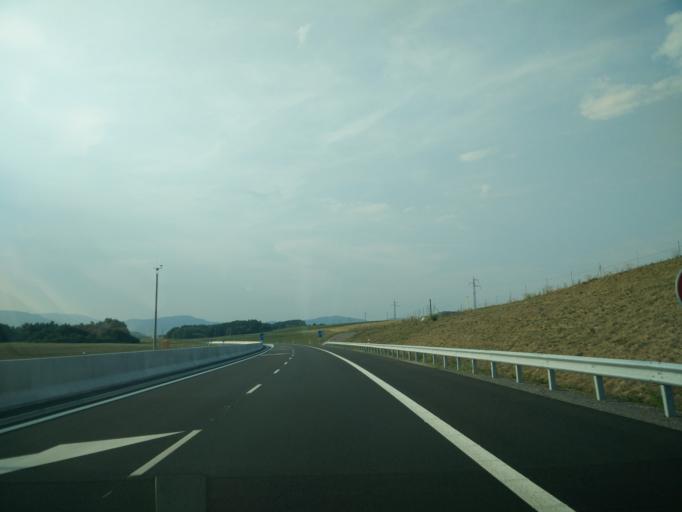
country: SK
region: Banskobystricky
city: Ziar nad Hronom
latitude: 48.5868
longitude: 18.8334
